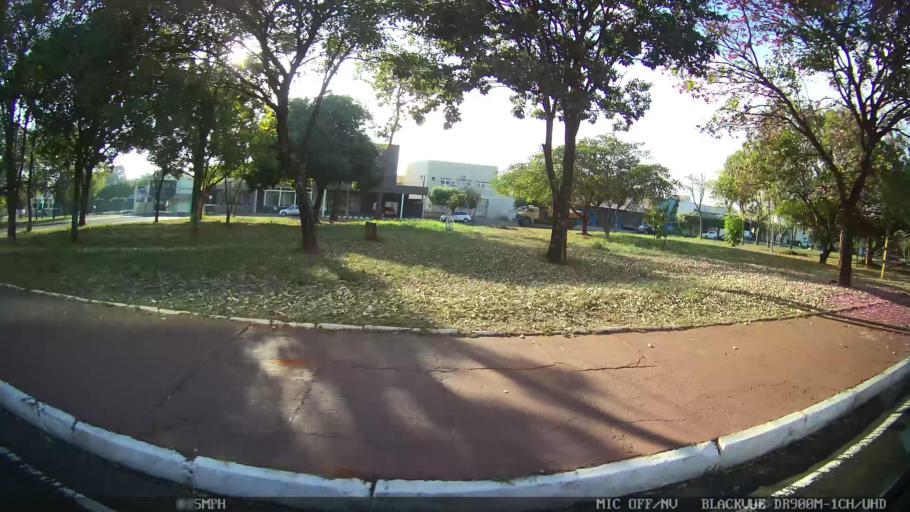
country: BR
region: Sao Paulo
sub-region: Sao Jose Do Rio Preto
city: Sao Jose do Rio Preto
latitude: -20.8319
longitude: -49.3660
